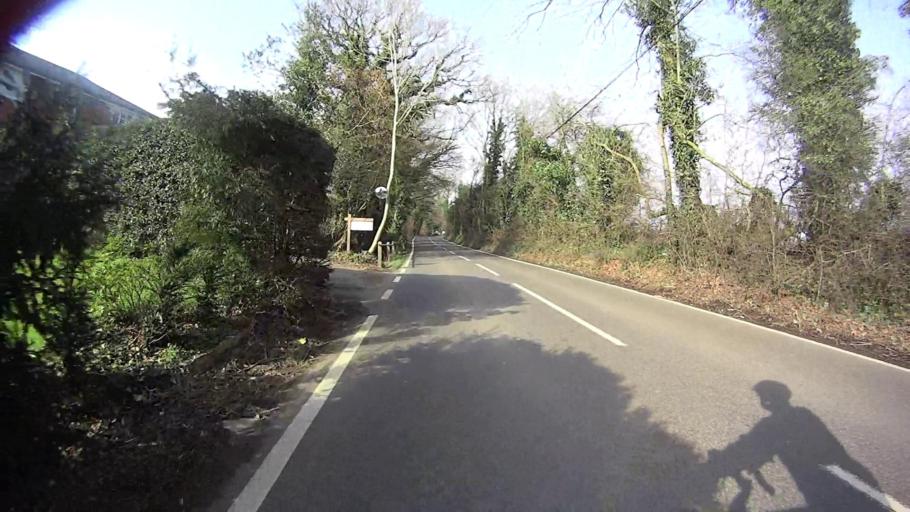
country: GB
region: England
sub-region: West Sussex
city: Copthorne
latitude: 51.1810
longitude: -0.0880
